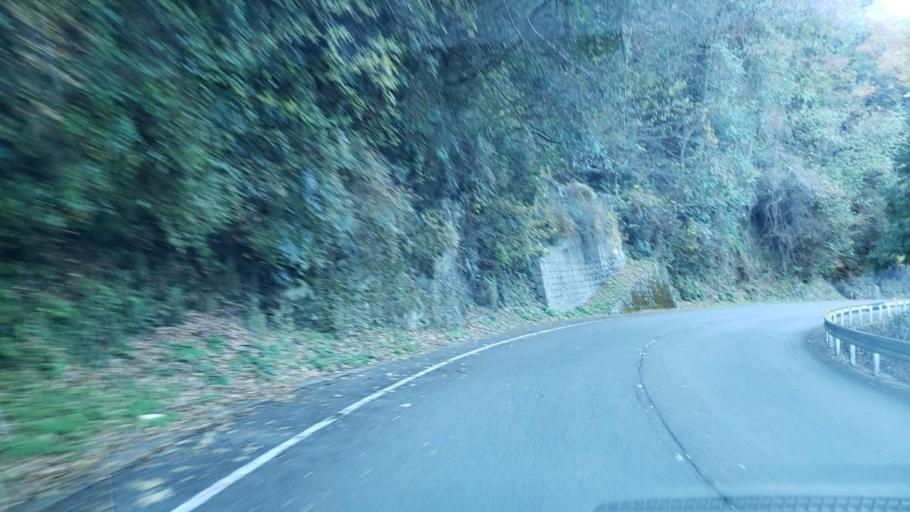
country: JP
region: Tokushima
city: Wakimachi
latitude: 34.0133
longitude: 134.0313
